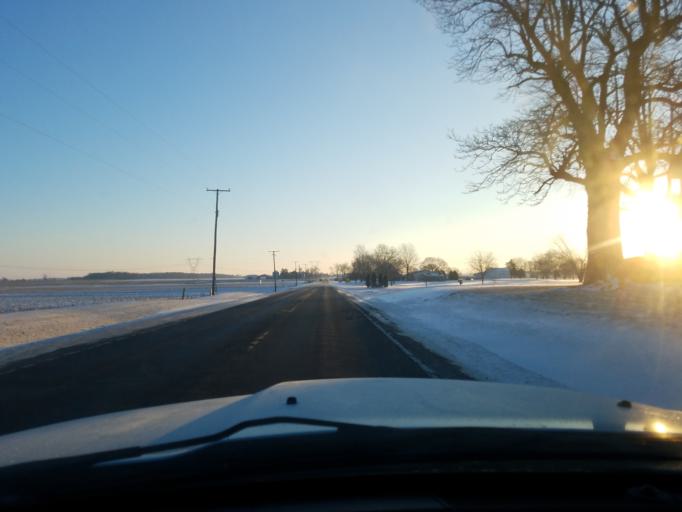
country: US
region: Indiana
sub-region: Marshall County
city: Bremen
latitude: 41.4498
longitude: -86.2445
